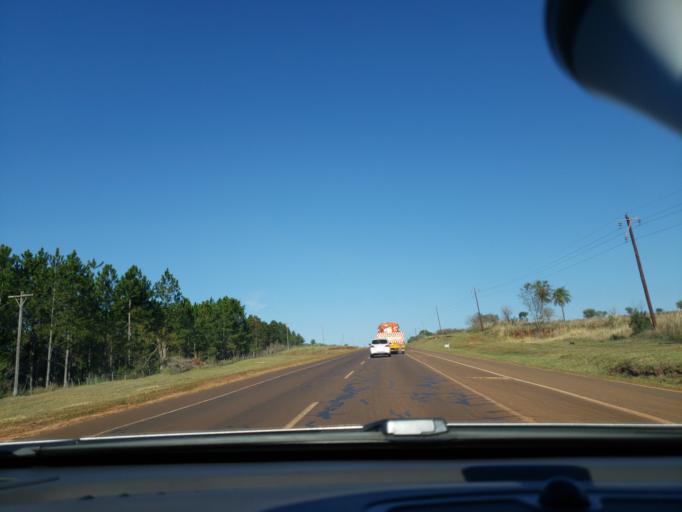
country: AR
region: Misiones
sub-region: Departamento de Apostoles
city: San Jose
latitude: -27.7538
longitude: -55.7767
